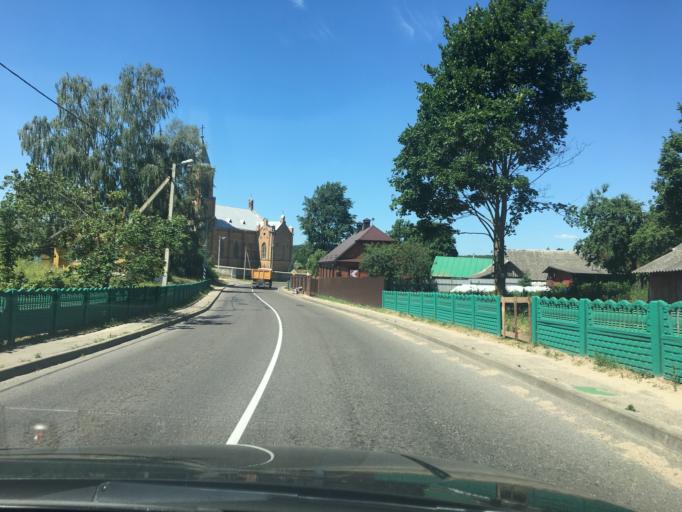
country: BY
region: Grodnenskaya
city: Hal'shany
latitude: 54.1548
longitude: 25.9091
